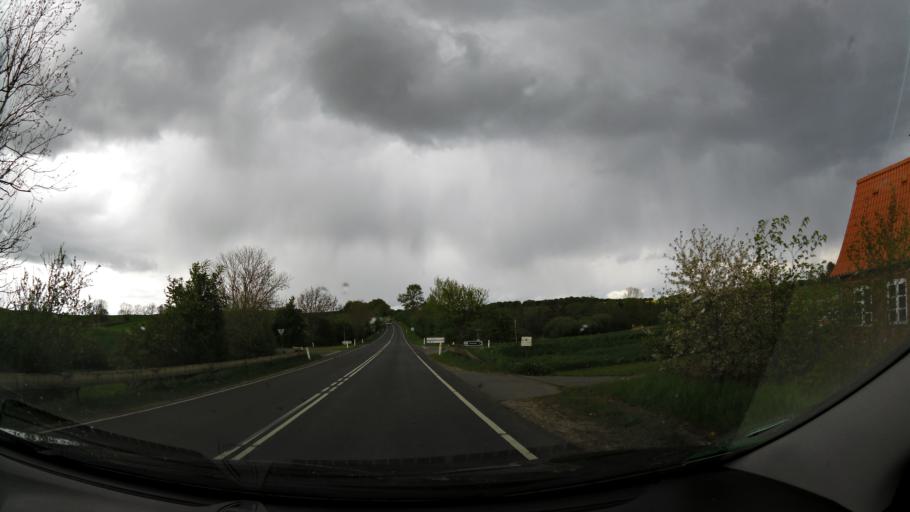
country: DK
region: South Denmark
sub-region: Nyborg Kommune
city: Nyborg
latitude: 55.2547
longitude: 10.7592
